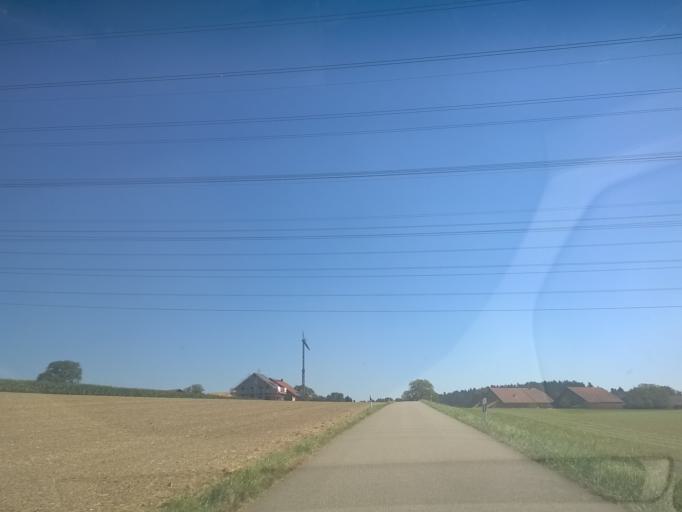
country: CH
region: Zurich
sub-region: Bezirk Winterthur
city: Brutten
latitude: 47.4839
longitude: 8.6551
